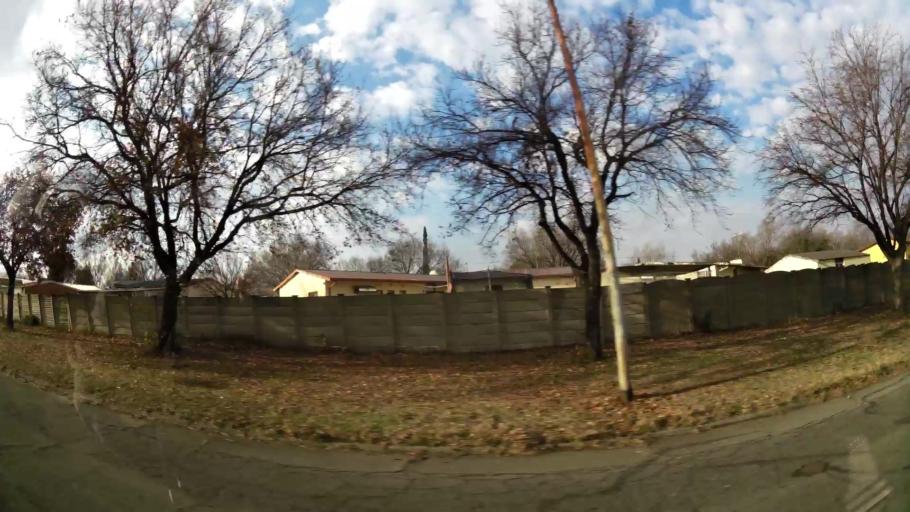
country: ZA
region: Orange Free State
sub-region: Fezile Dabi District Municipality
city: Sasolburg
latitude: -26.8245
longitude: 27.8125
